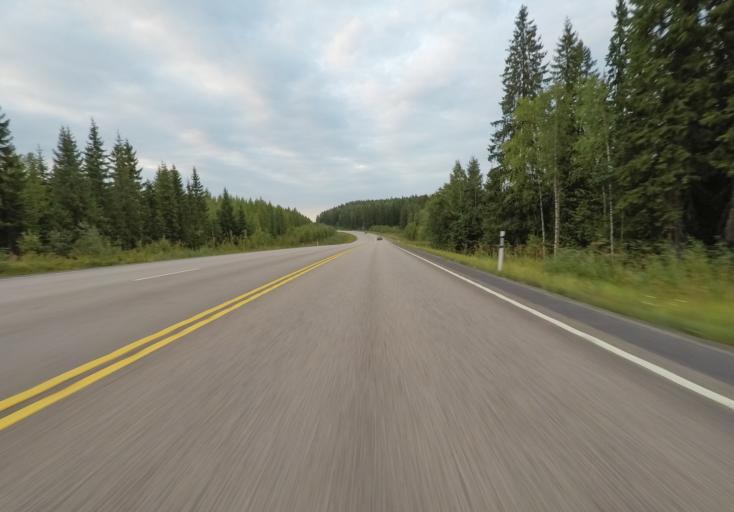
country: FI
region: Central Finland
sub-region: Jyvaeskylae
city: Toivakka
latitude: 62.0396
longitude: 26.0497
